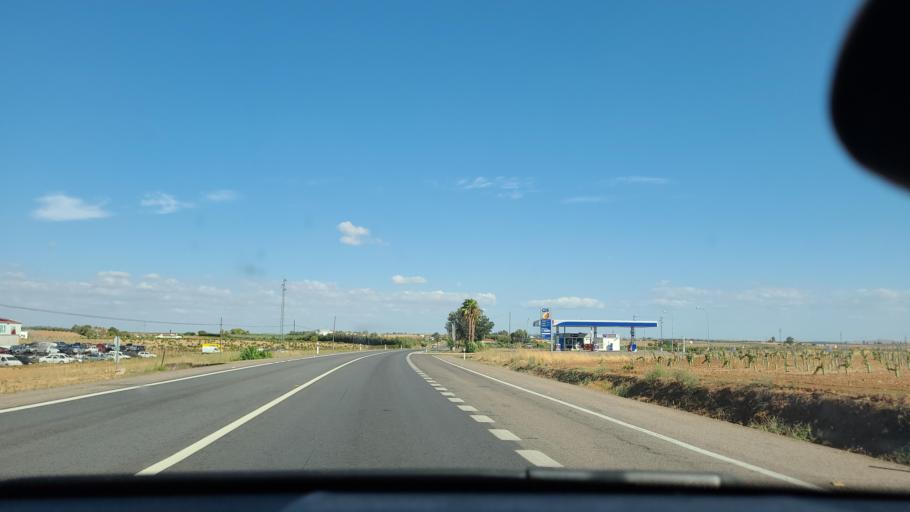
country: ES
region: Extremadura
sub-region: Provincia de Badajoz
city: Puebla de Sancho Perez
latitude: 38.4047
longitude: -6.3618
